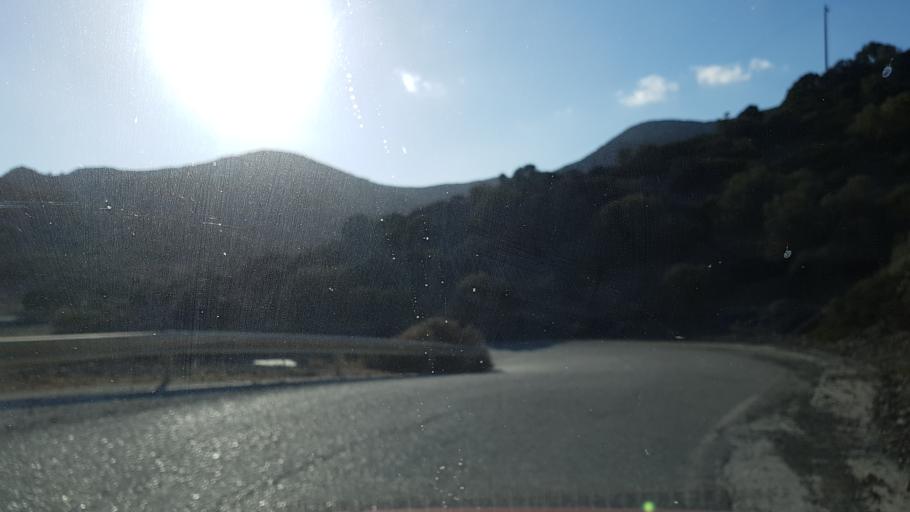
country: GR
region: Crete
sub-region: Nomos Irakleiou
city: Moires
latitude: 34.9362
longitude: 24.8081
